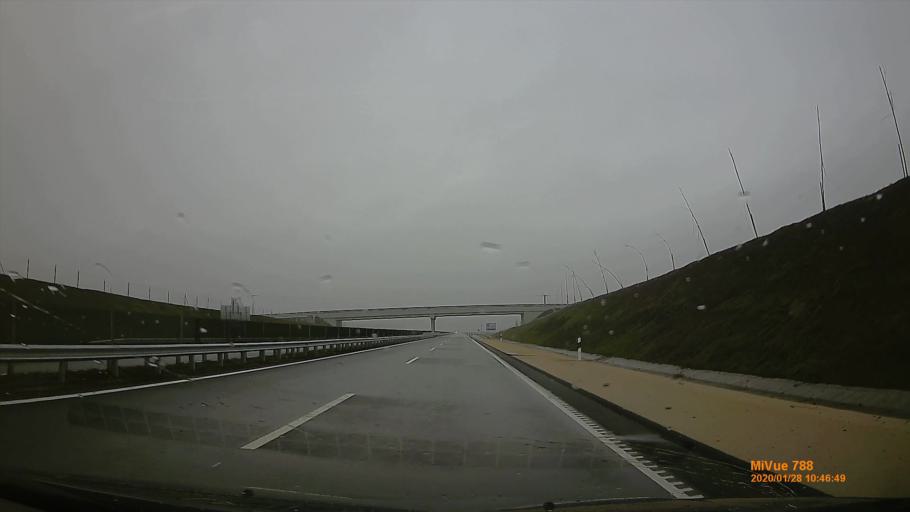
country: HU
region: Pest
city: Monor
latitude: 47.3688
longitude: 19.4776
